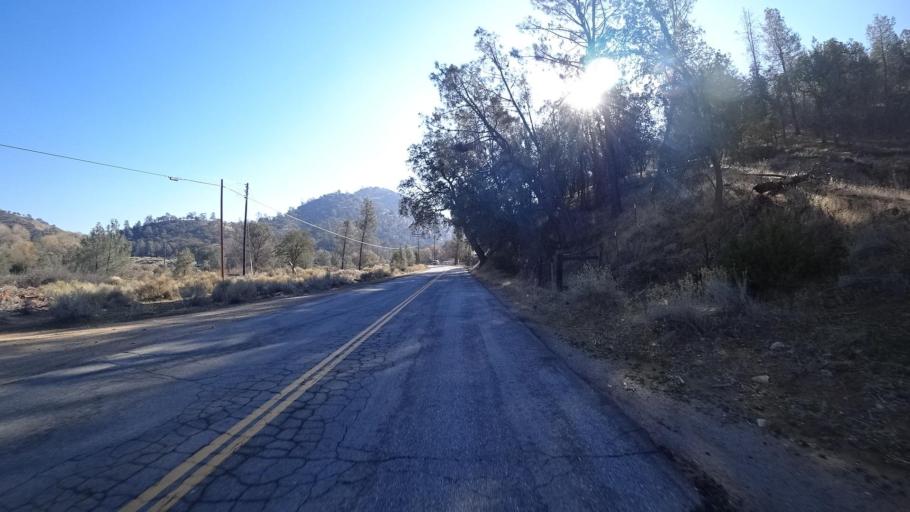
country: US
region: California
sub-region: Kern County
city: Golden Hills
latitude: 35.3054
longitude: -118.4389
